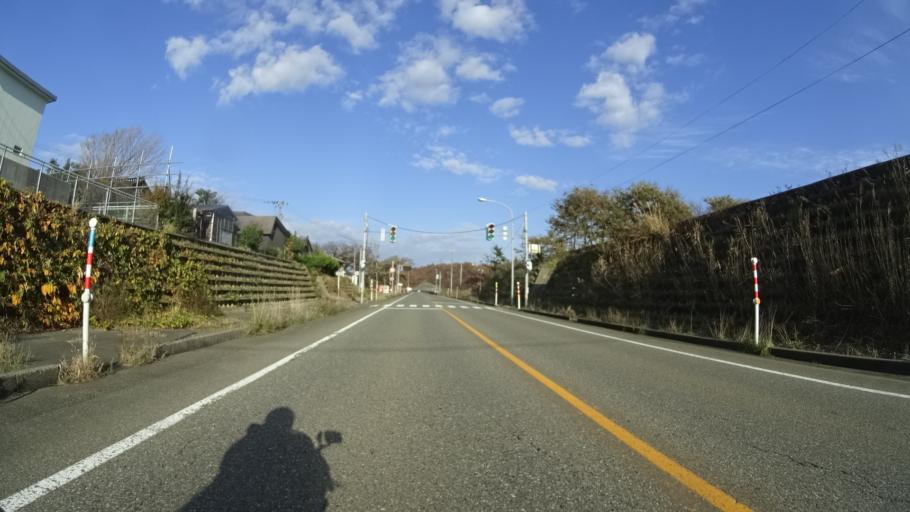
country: JP
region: Niigata
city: Kashiwazaki
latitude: 37.3446
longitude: 138.4849
